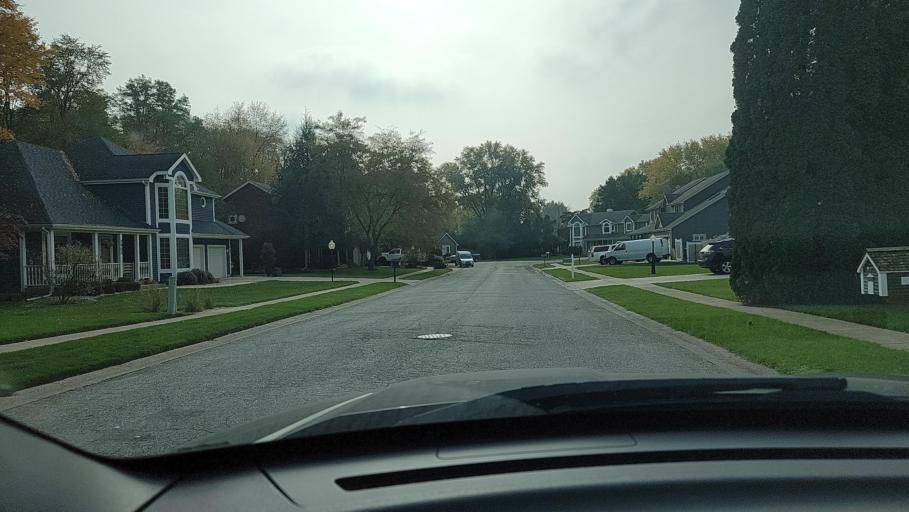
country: US
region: Indiana
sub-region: Porter County
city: Portage
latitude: 41.5937
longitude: -87.1796
